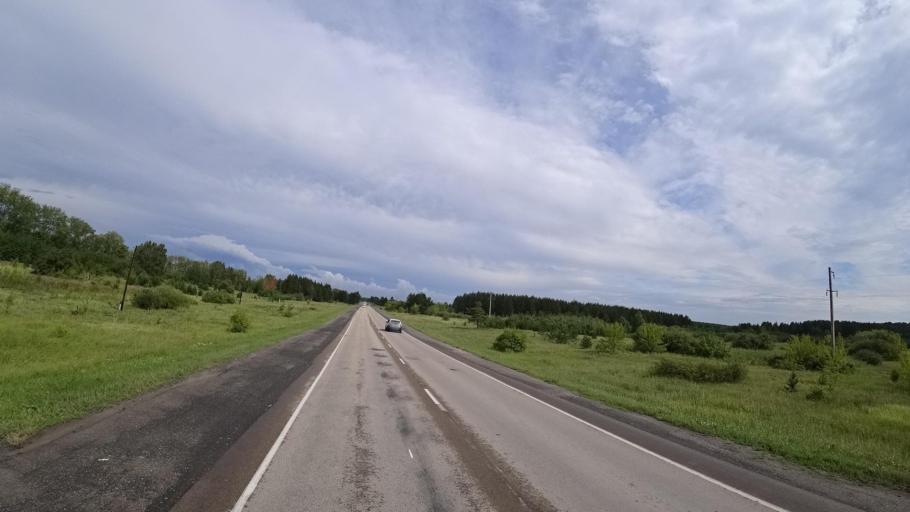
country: RU
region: Sverdlovsk
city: Kamyshlov
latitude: 56.8434
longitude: 62.7750
